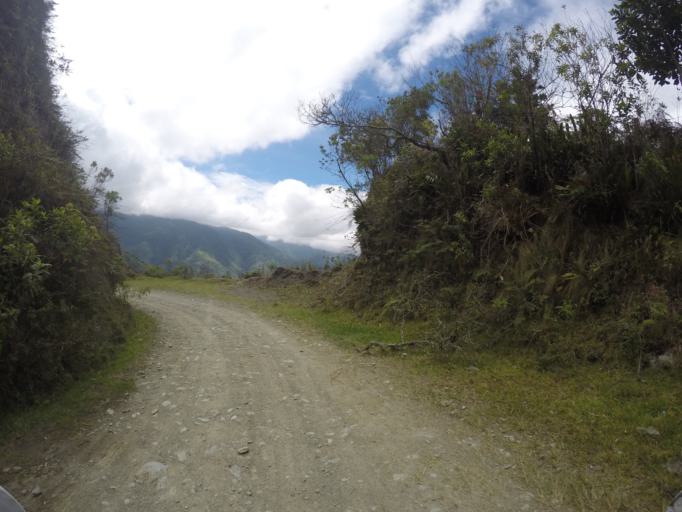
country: CO
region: Tolima
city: Cajamarca
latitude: 4.5315
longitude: -75.4348
